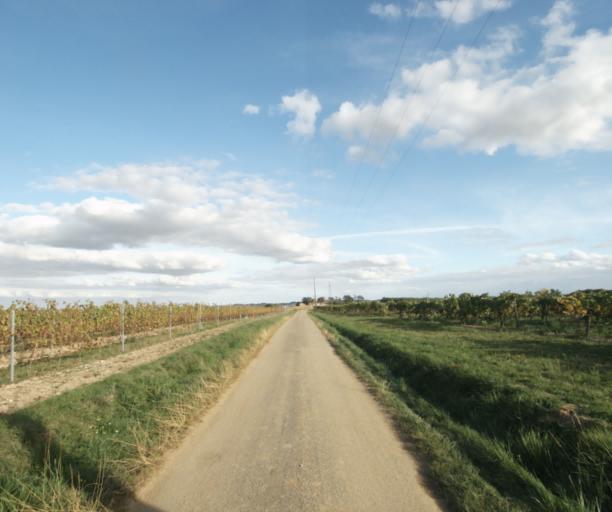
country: FR
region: Midi-Pyrenees
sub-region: Departement du Gers
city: Gondrin
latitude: 43.9003
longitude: 0.2561
